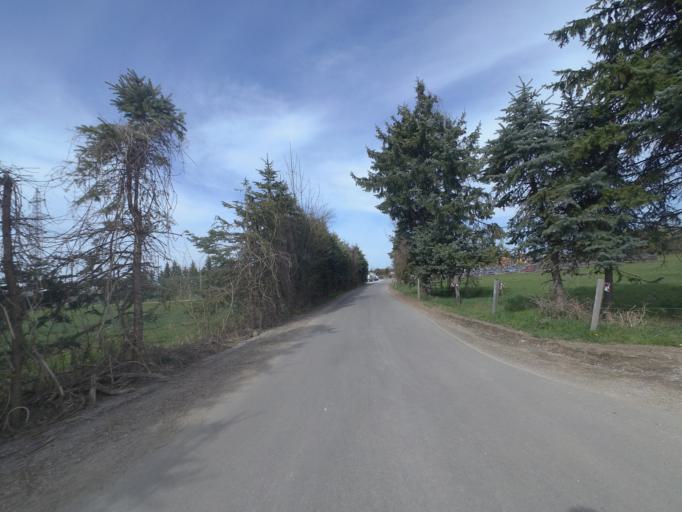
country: DE
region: Bavaria
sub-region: Upper Bavaria
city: Ainring
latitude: 47.8061
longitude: 12.9794
